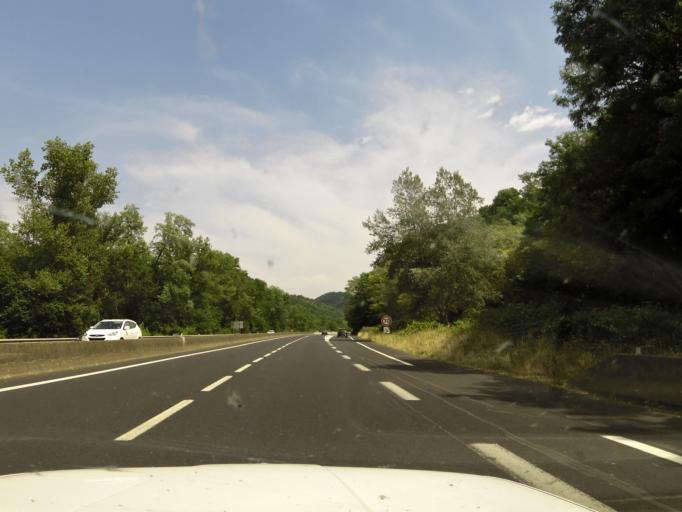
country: FR
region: Auvergne
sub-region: Departement du Puy-de-Dome
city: Issoire
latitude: 45.5937
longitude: 3.2309
